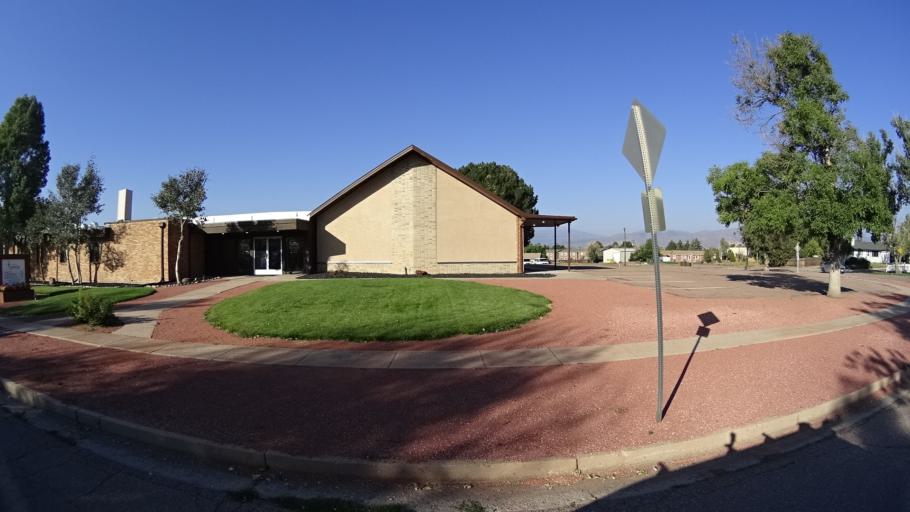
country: US
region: Colorado
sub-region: El Paso County
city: Cimarron Hills
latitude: 38.8937
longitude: -104.7467
